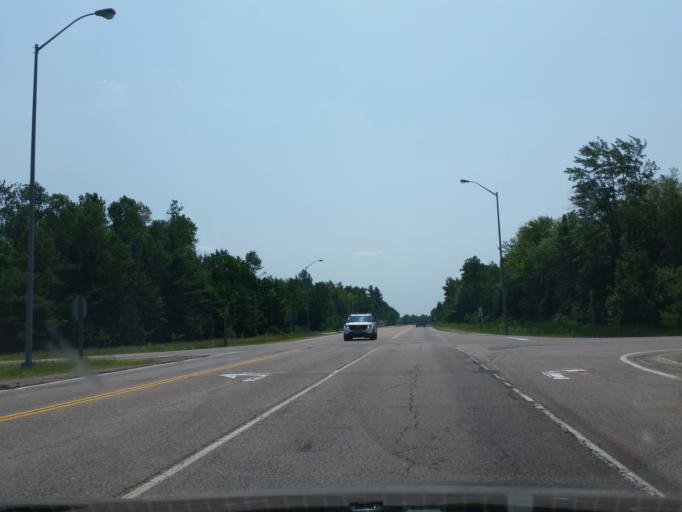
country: CA
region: Ontario
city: Petawawa
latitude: 45.8807
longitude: -77.3036
